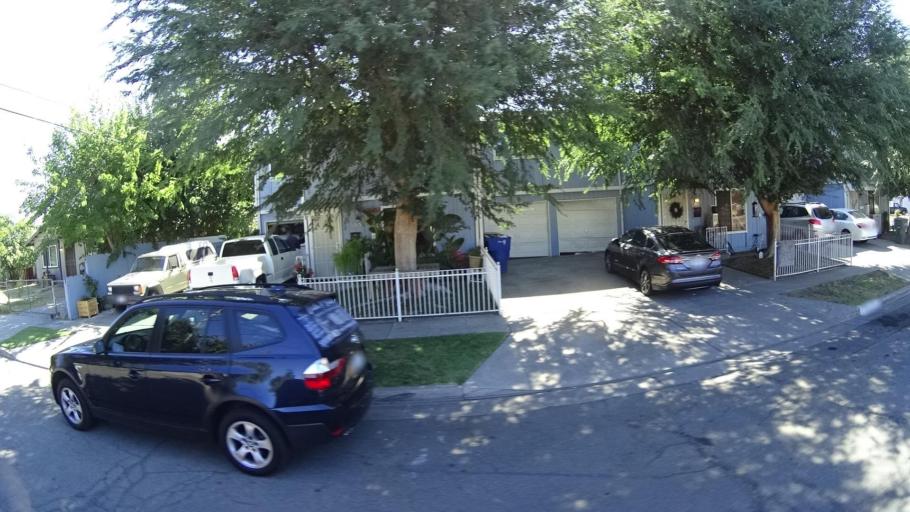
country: US
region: California
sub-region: Fresno County
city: Fresno
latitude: 36.7845
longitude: -119.7928
